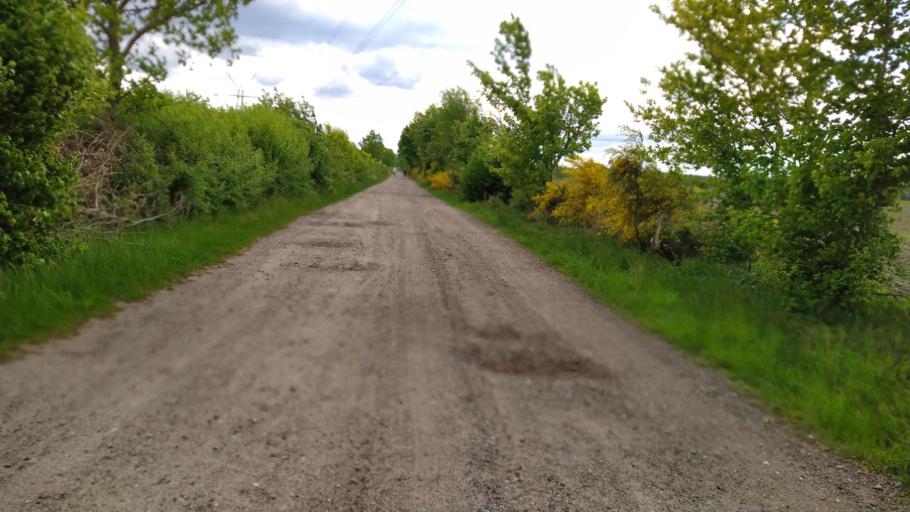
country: DE
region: Lower Saxony
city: Ahlerstedt
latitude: 53.3793
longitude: 9.3983
